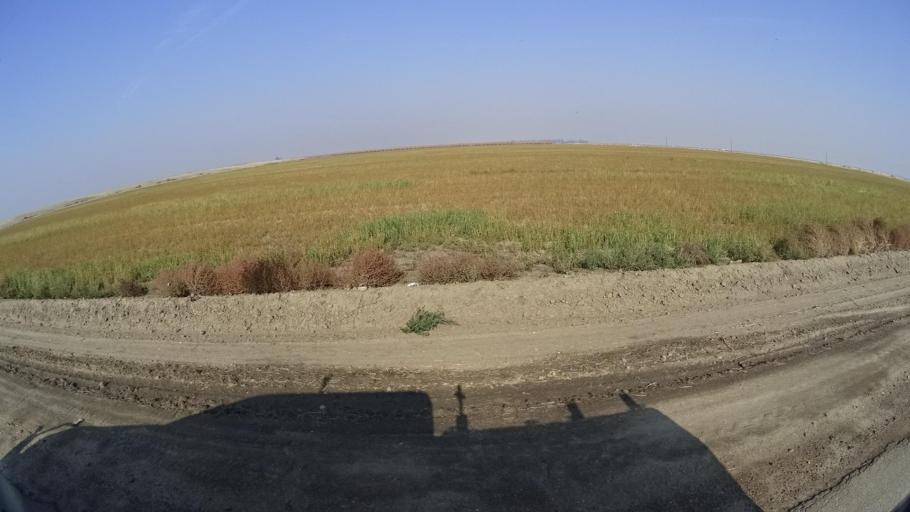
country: US
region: California
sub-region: Kern County
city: Buttonwillow
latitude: 35.3331
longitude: -119.3746
